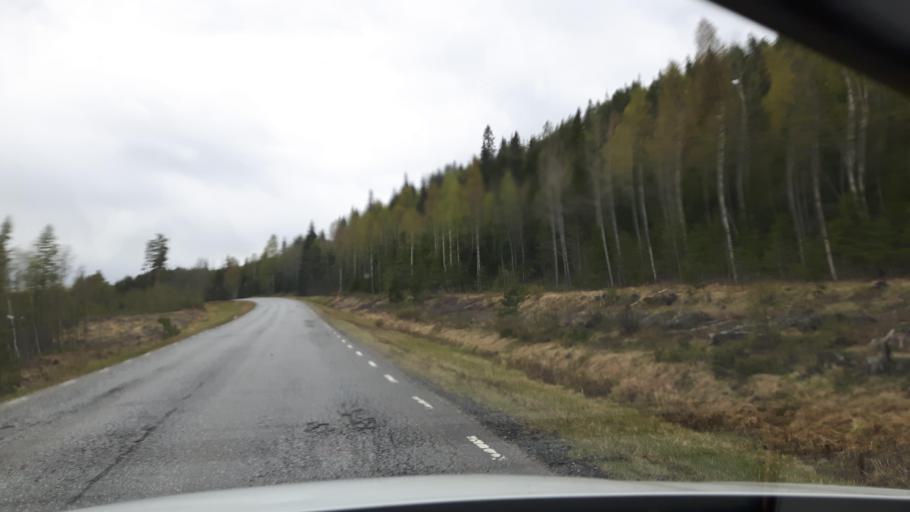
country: SE
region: Vaesterbotten
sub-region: Skelleftea Kommun
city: Burtraesk
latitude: 64.2858
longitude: 20.5270
